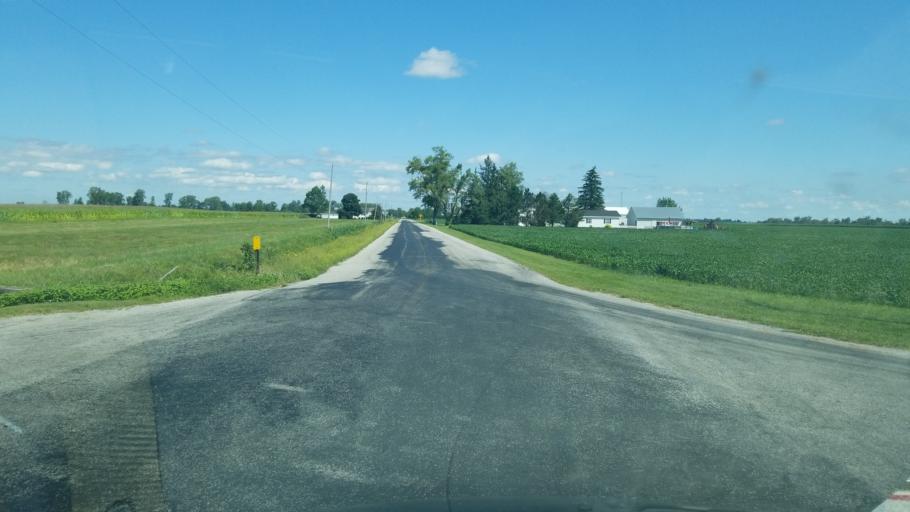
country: US
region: Ohio
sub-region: Henry County
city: Deshler
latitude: 41.2692
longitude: -83.8439
